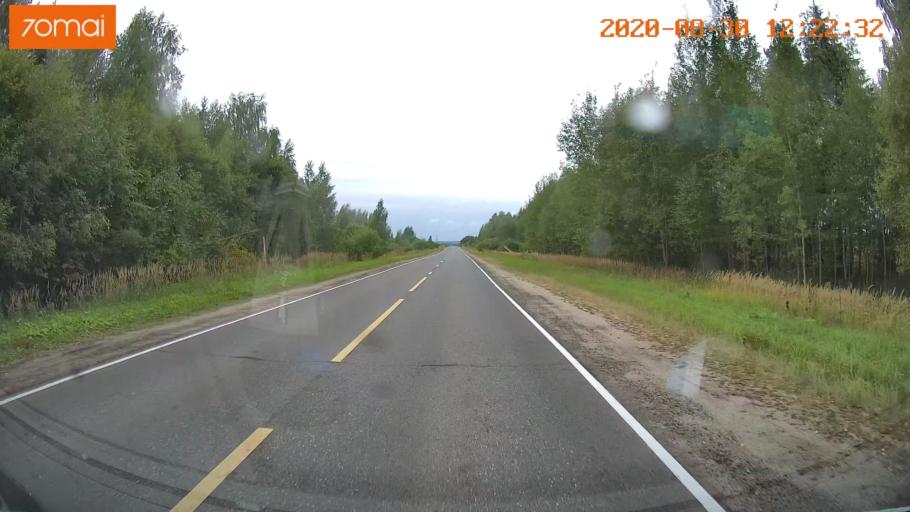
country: RU
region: Ivanovo
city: Yur'yevets
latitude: 57.3300
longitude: 42.8476
